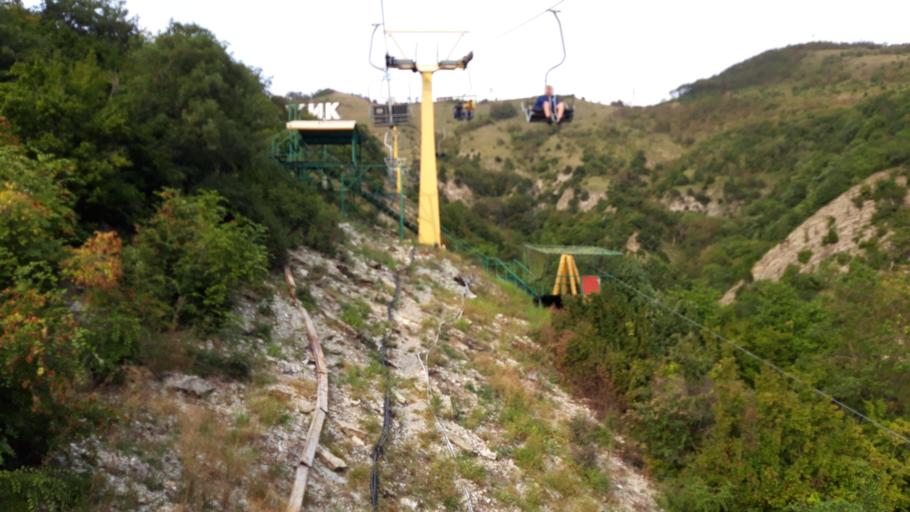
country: RU
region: Krasnodarskiy
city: Gelendzhik
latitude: 44.5806
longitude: 38.0964
